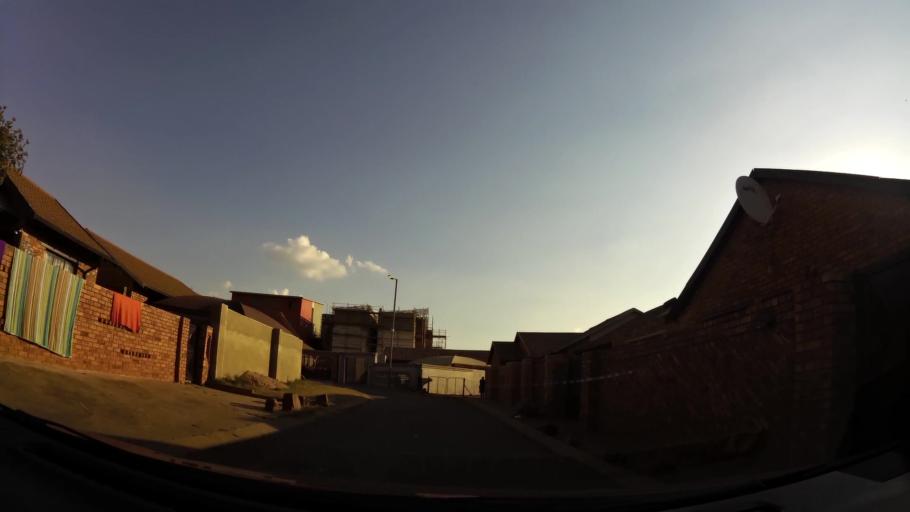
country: ZA
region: Gauteng
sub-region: City of Johannesburg Metropolitan Municipality
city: Soweto
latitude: -26.2272
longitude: 27.8563
